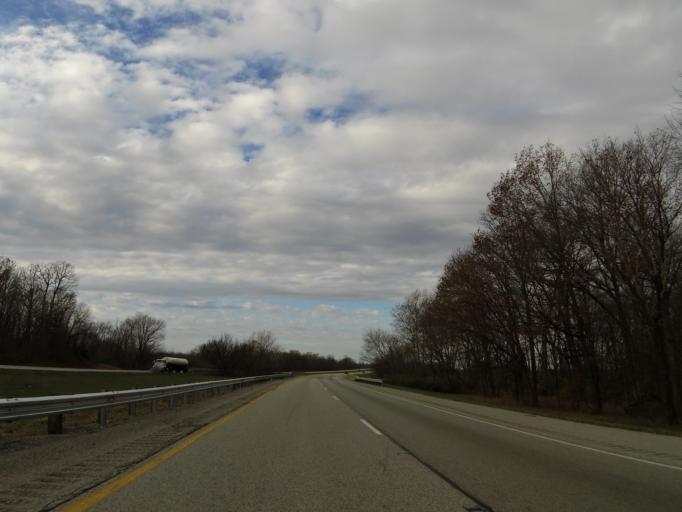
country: US
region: Illinois
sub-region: Washington County
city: Nashville
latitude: 38.3904
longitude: -89.3249
